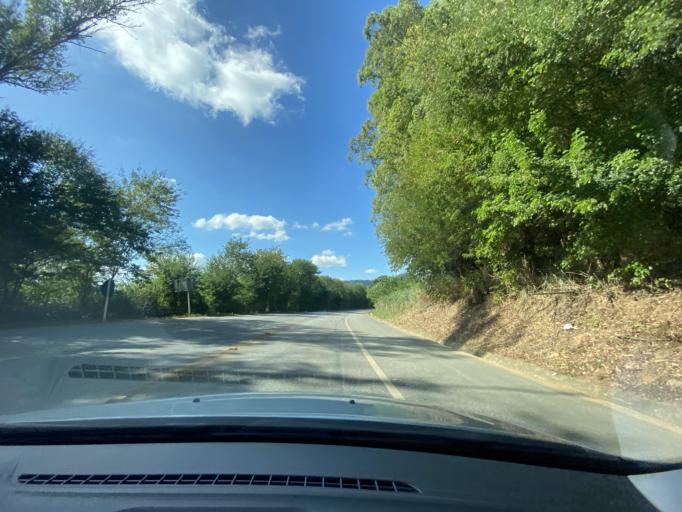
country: BR
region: Espirito Santo
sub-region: Jeronimo Monteiro
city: Jeronimo Monteiro
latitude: -20.7825
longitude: -41.4129
